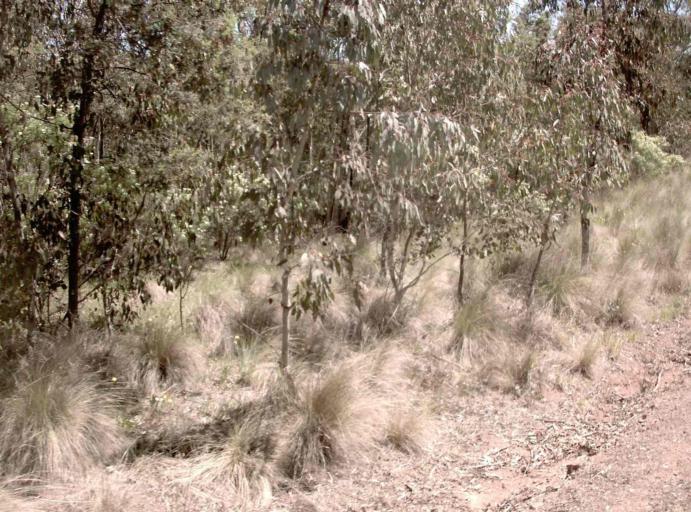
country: AU
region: New South Wales
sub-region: Snowy River
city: Jindabyne
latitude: -37.0781
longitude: 148.2604
